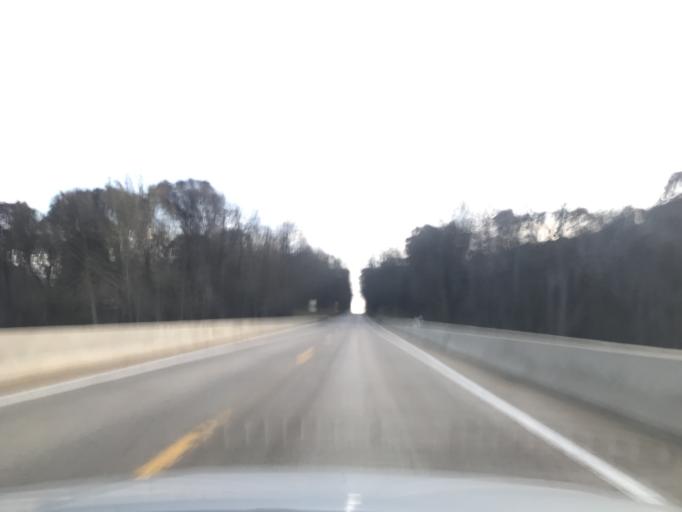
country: US
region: Illinois
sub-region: Henderson County
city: Oquawka
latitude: 41.0024
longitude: -90.8536
